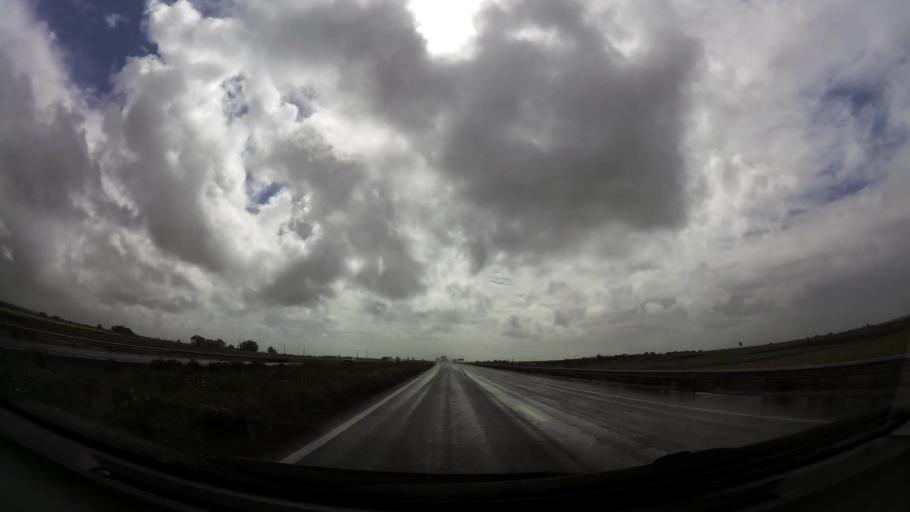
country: MA
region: Grand Casablanca
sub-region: Nouaceur
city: Dar Bouazza
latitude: 33.3760
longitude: -7.9093
